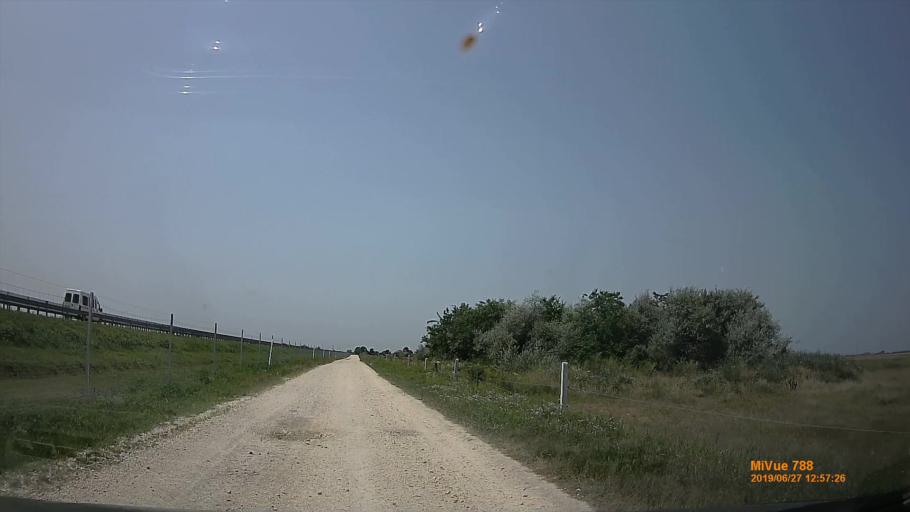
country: HU
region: Pest
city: Cegled
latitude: 47.1916
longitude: 19.8594
